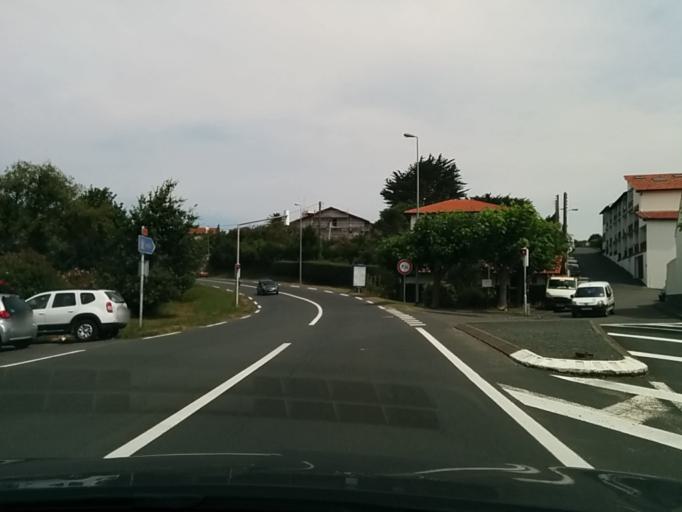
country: FR
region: Aquitaine
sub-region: Departement des Pyrenees-Atlantiques
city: Ciboure
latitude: 43.3915
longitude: -1.6861
